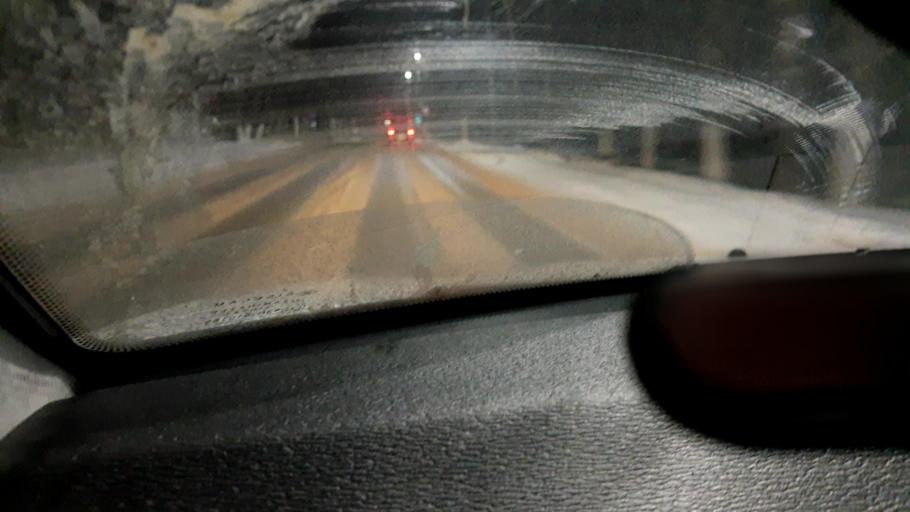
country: RU
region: Nizjnij Novgorod
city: Bogorodsk
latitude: 56.1004
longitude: 43.4970
